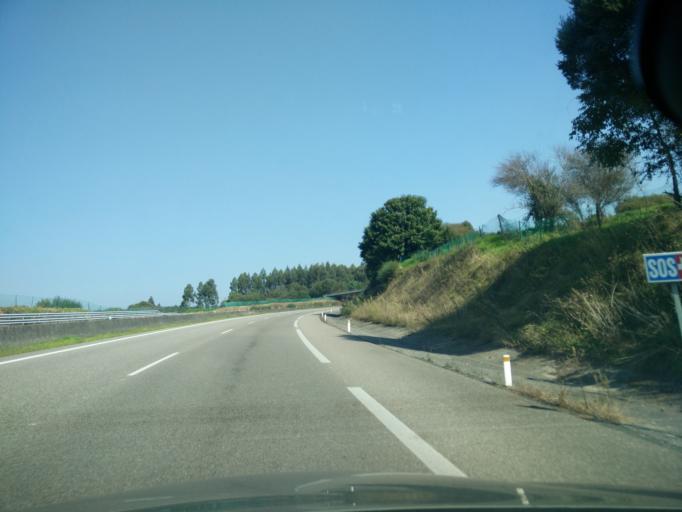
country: ES
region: Galicia
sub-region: Provincia da Coruna
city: Mino
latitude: 43.3606
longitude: -8.2021
